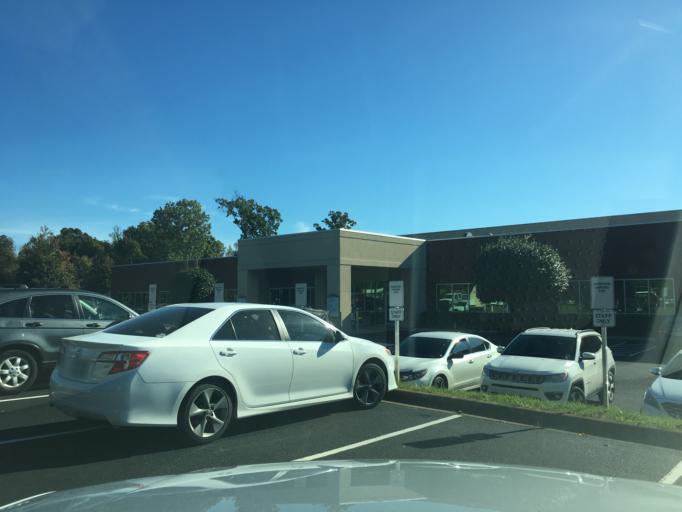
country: US
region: North Carolina
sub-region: Catawba County
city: Hickory
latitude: 35.7307
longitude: -81.3101
